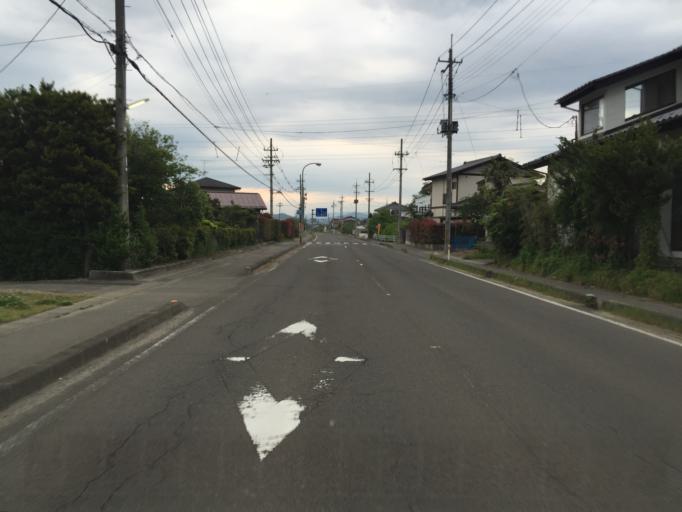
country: JP
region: Fukushima
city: Fukushima-shi
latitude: 37.8116
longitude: 140.4715
